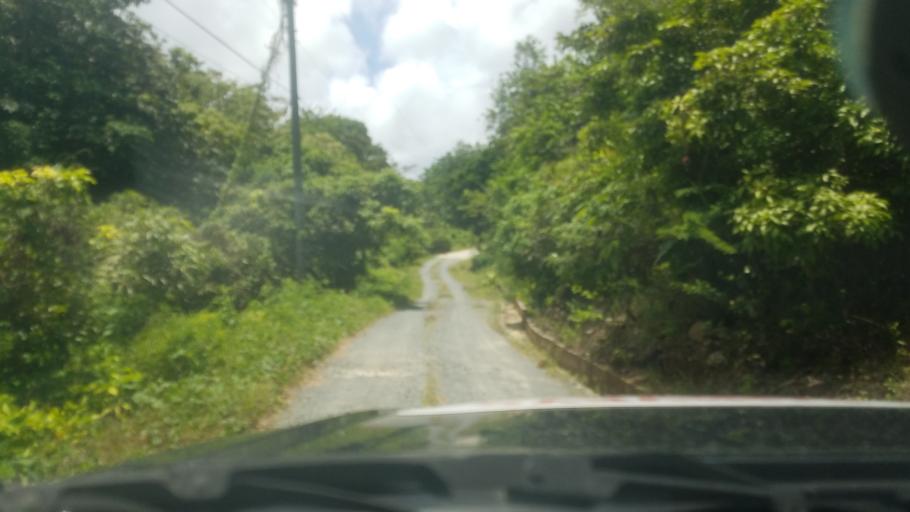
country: LC
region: Praslin
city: Praslin
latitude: 13.8663
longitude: -60.9086
